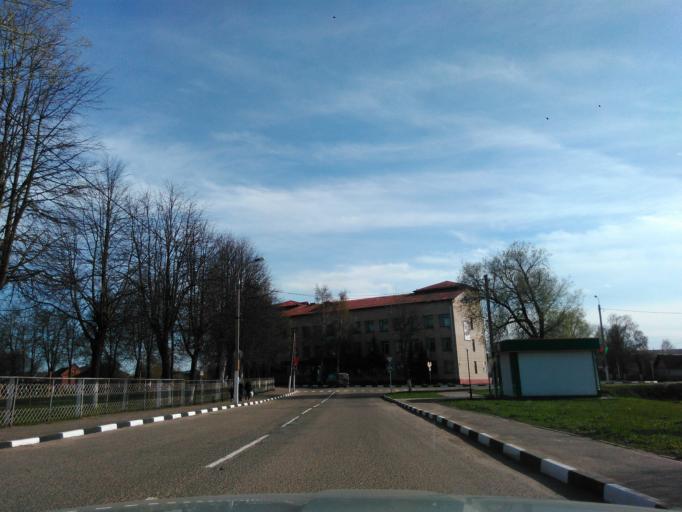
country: BY
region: Vitebsk
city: Chashniki
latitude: 54.8604
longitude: 29.1635
